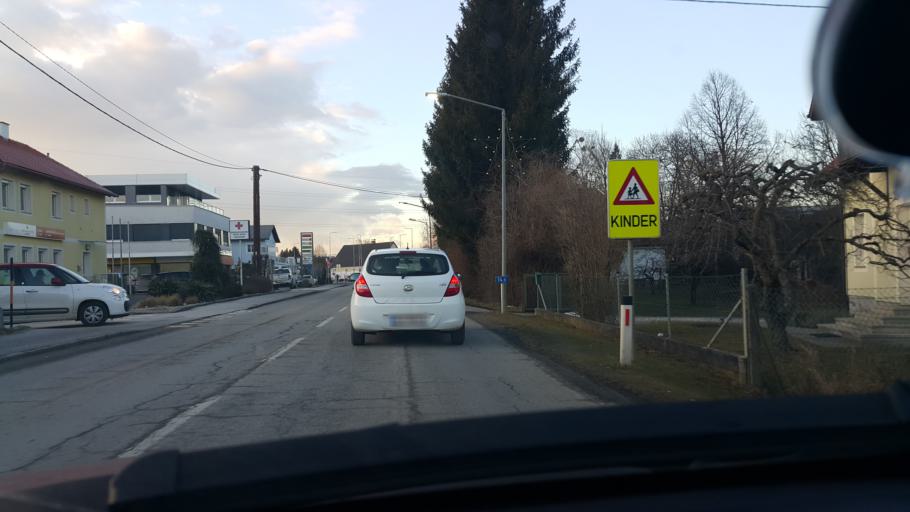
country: AT
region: Styria
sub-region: Politischer Bezirk Graz-Umgebung
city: Lieboch
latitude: 46.9733
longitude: 15.3373
